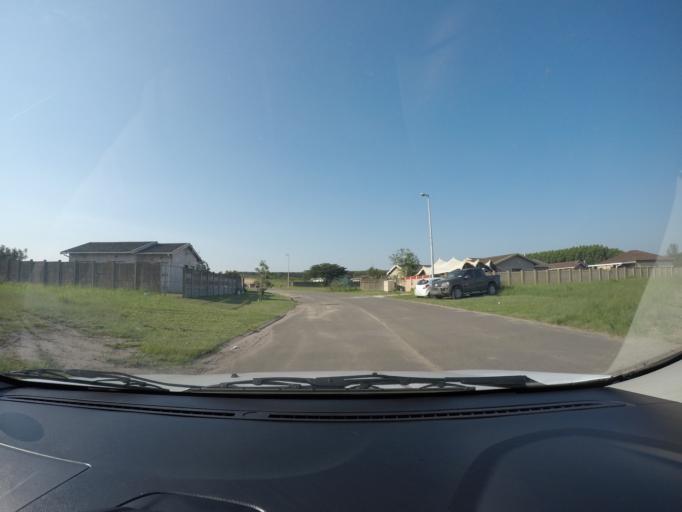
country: ZA
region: KwaZulu-Natal
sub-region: uThungulu District Municipality
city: Richards Bay
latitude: -28.7113
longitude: 32.0373
